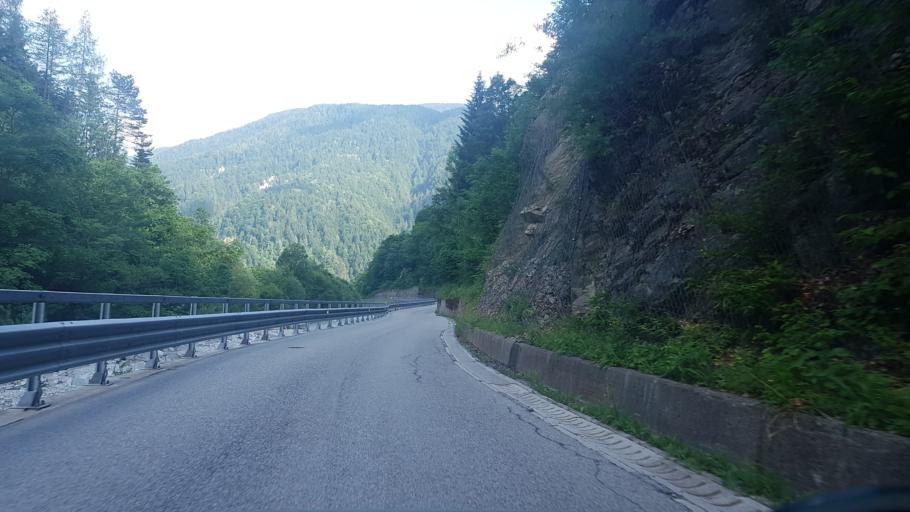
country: IT
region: Friuli Venezia Giulia
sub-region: Provincia di Udine
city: Pontebba
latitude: 46.5125
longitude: 13.2960
